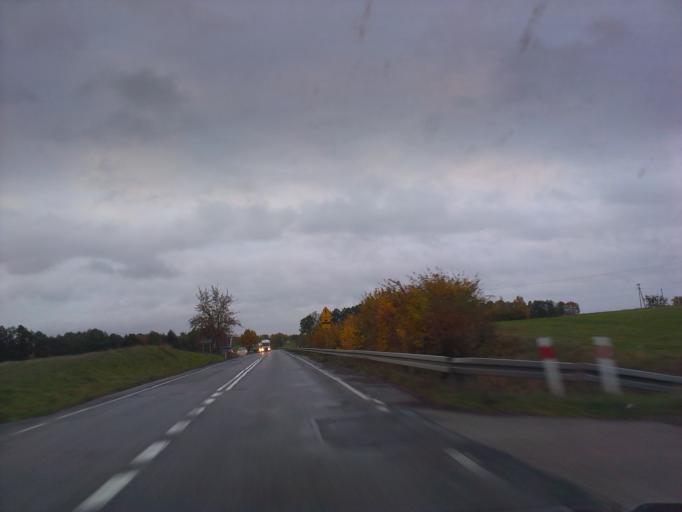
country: PL
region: Kujawsko-Pomorskie
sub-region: Powiat tucholski
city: Lubiewo
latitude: 53.5102
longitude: 17.9751
